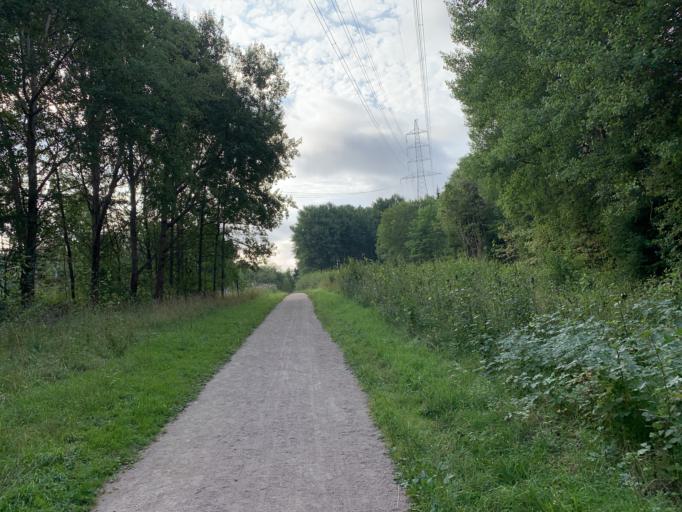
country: SE
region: Stockholm
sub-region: Solna Kommun
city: Rasunda
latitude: 59.3903
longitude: 17.9872
